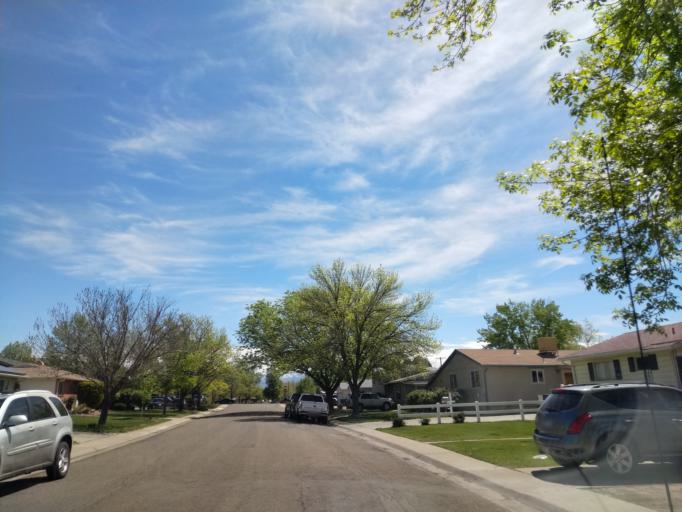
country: US
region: Colorado
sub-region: Mesa County
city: Grand Junction
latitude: 39.0800
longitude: -108.5723
